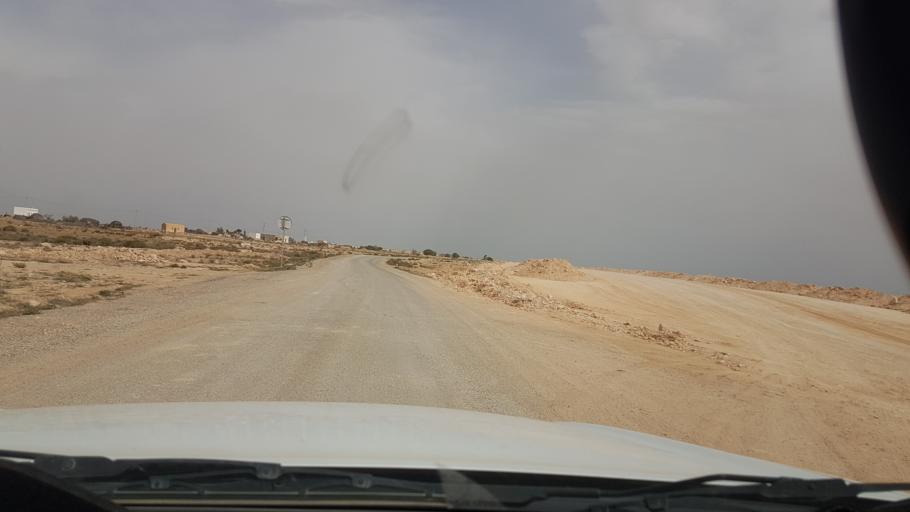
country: TN
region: Madanin
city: Medenine
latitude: 33.3027
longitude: 10.6107
